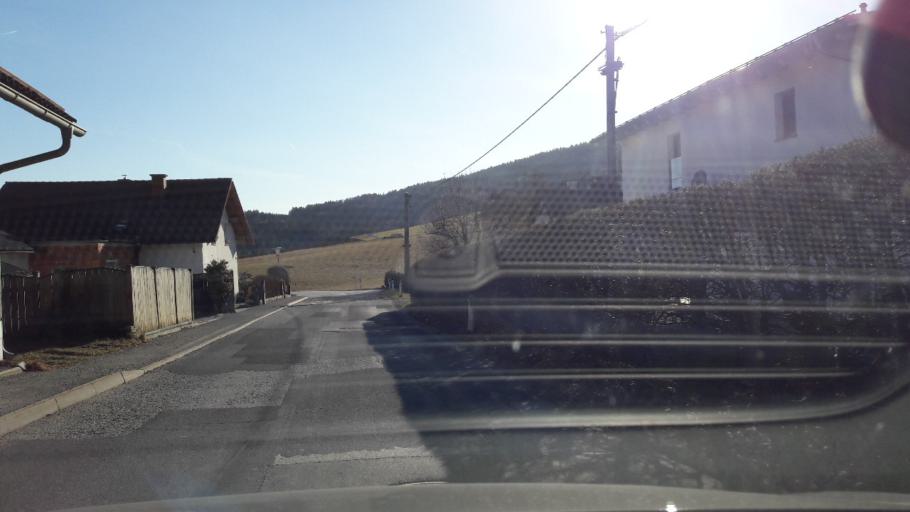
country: AT
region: Styria
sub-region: Politischer Bezirk Graz-Umgebung
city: Eisbach
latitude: 47.1283
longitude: 15.2881
